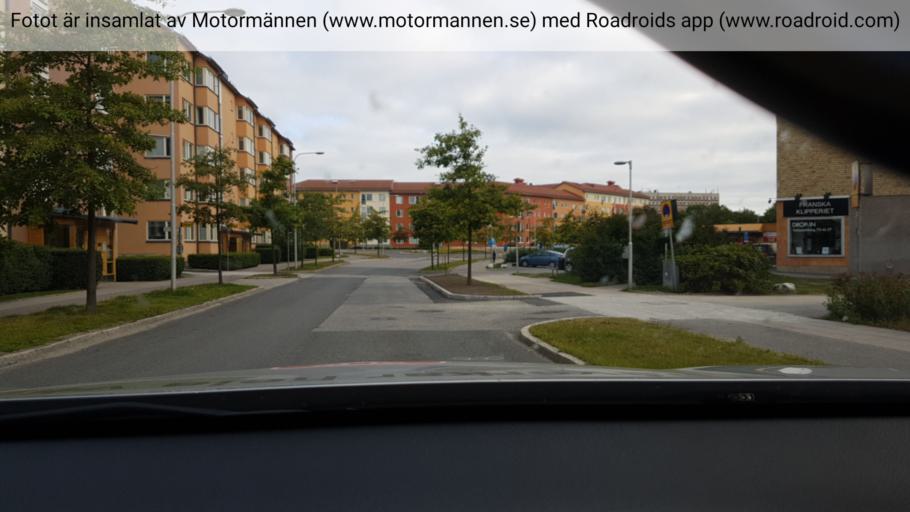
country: SE
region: Stockholm
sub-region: Huddinge Kommun
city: Huddinge
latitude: 59.2389
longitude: 17.9948
